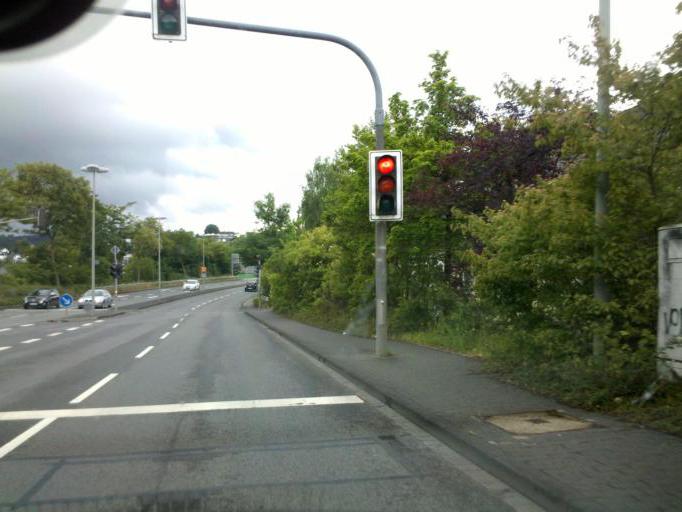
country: DE
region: North Rhine-Westphalia
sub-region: Regierungsbezirk Arnsberg
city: Meschede
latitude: 51.3514
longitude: 8.2800
